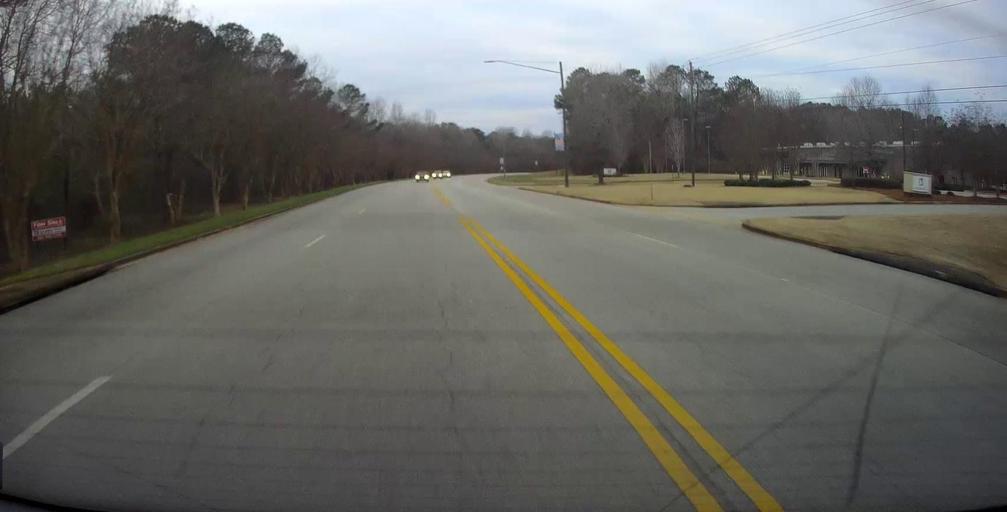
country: US
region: Alabama
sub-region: Chambers County
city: Valley
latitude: 32.8148
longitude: -85.1832
